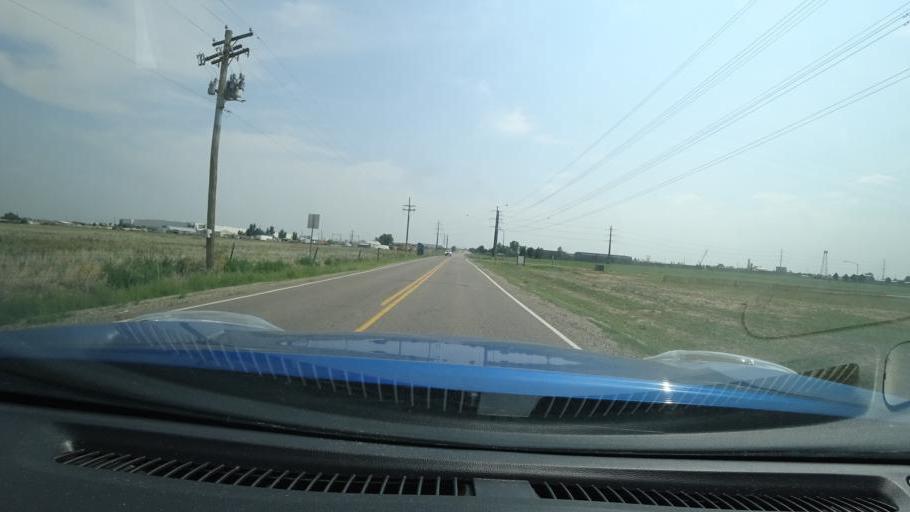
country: US
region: Colorado
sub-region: Adams County
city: Aurora
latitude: 39.7577
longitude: -104.7346
